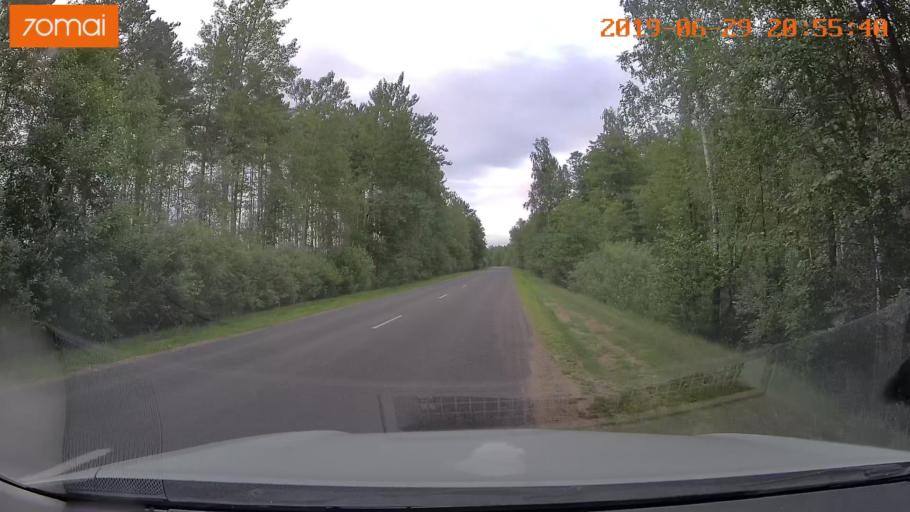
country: BY
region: Brest
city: Hantsavichy
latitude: 52.7025
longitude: 26.3659
